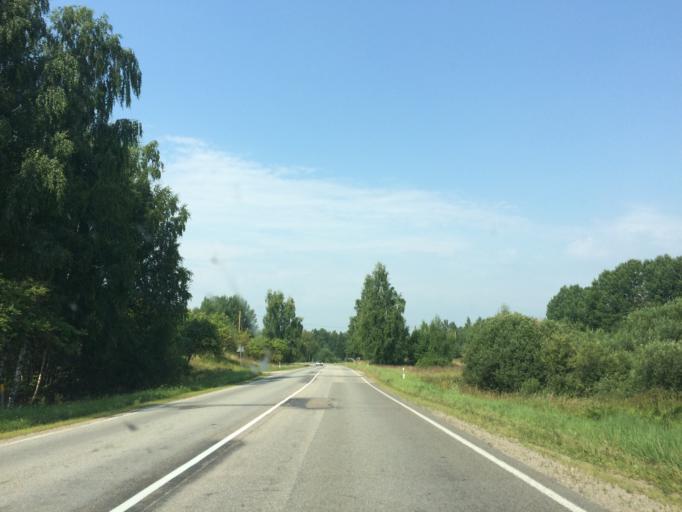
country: LV
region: Ludzas Rajons
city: Ludza
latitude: 56.5374
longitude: 27.5779
